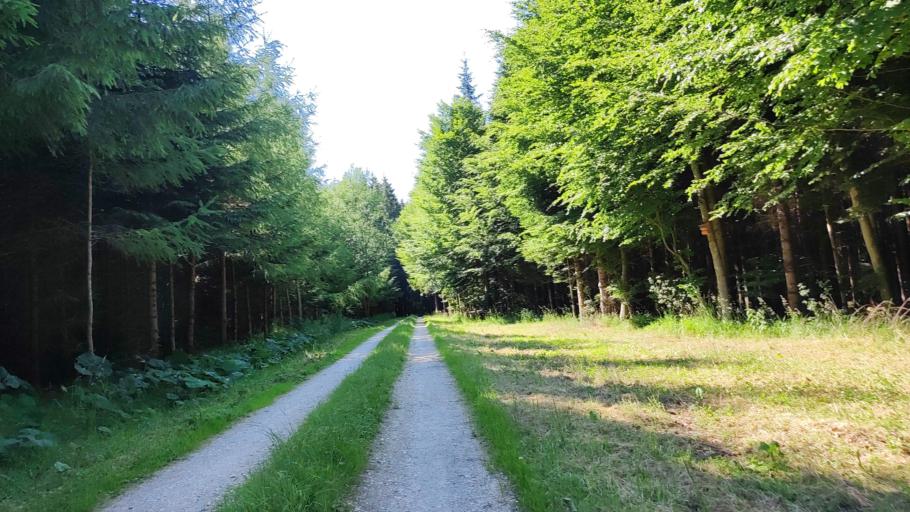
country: DE
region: Bavaria
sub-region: Swabia
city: Burtenbach
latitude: 48.3669
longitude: 10.4997
